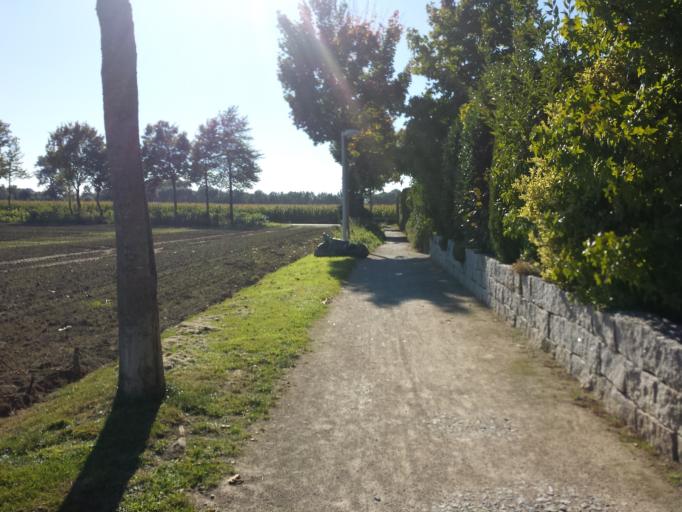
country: DE
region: North Rhine-Westphalia
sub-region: Regierungsbezirk Detmold
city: Langenberg
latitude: 51.7452
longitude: 8.3253
